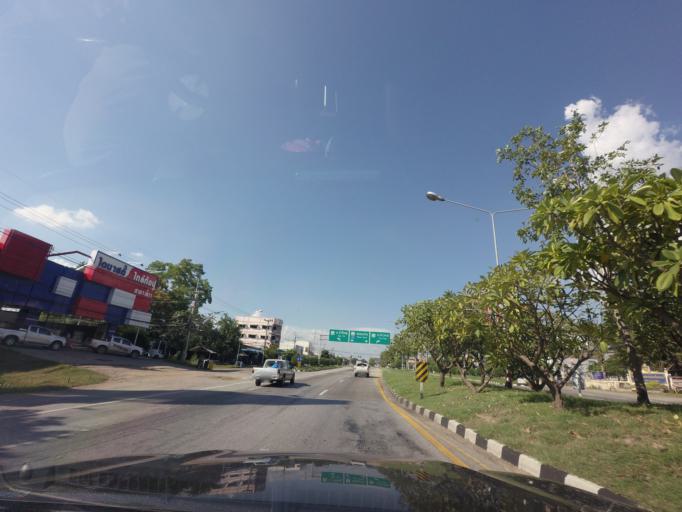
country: TH
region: Nakhon Ratchasima
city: Sida
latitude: 15.5456
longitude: 102.5475
